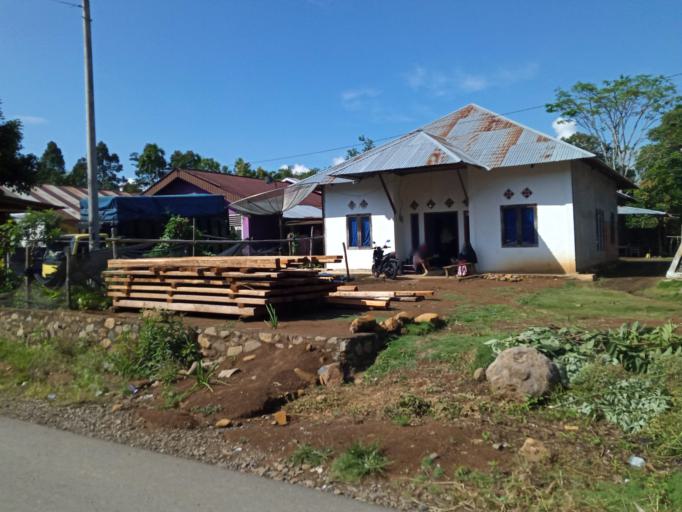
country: ID
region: Jambi
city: Sungai Penuh
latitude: -2.1913
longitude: 101.6131
